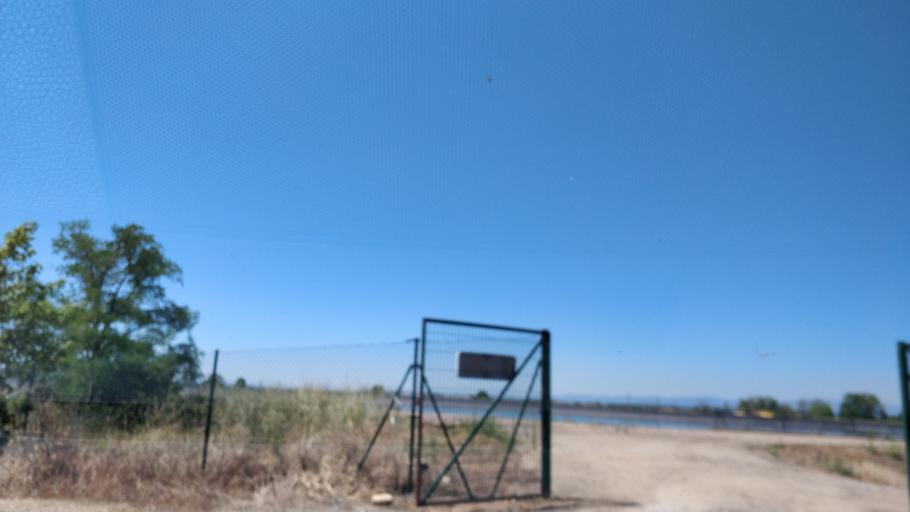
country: ES
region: Castille and Leon
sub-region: Provincia de Leon
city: Bustillo del Paramo
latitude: 42.4804
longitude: -5.8071
